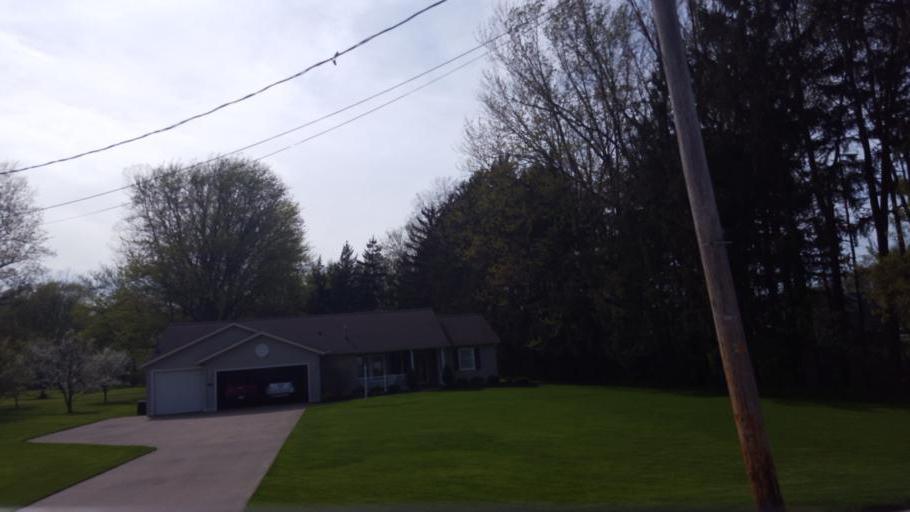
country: US
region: Ohio
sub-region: Lake County
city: Perry
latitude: 41.7977
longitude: -81.1045
